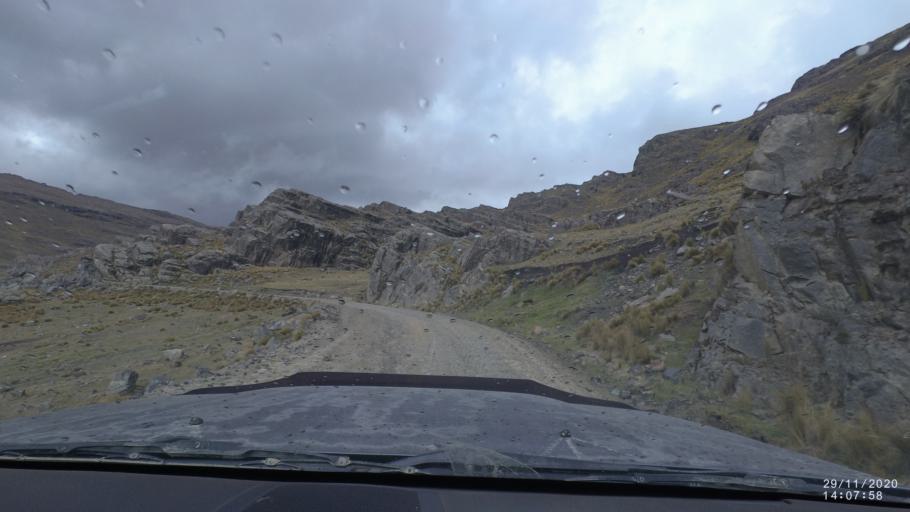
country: BO
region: Cochabamba
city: Sipe Sipe
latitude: -17.2210
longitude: -66.3851
